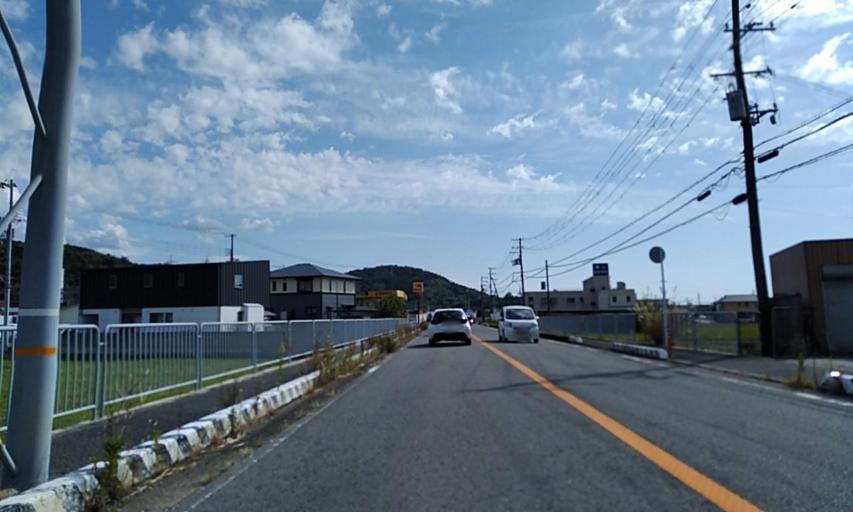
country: JP
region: Wakayama
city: Gobo
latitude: 33.9230
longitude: 135.1448
